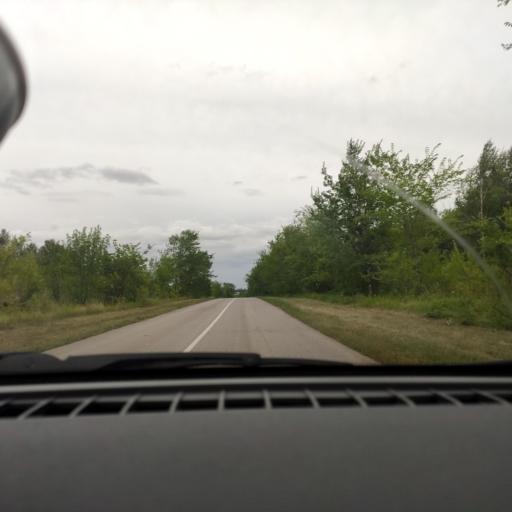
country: RU
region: Samara
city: Georgiyevka
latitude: 53.5118
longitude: 50.9913
